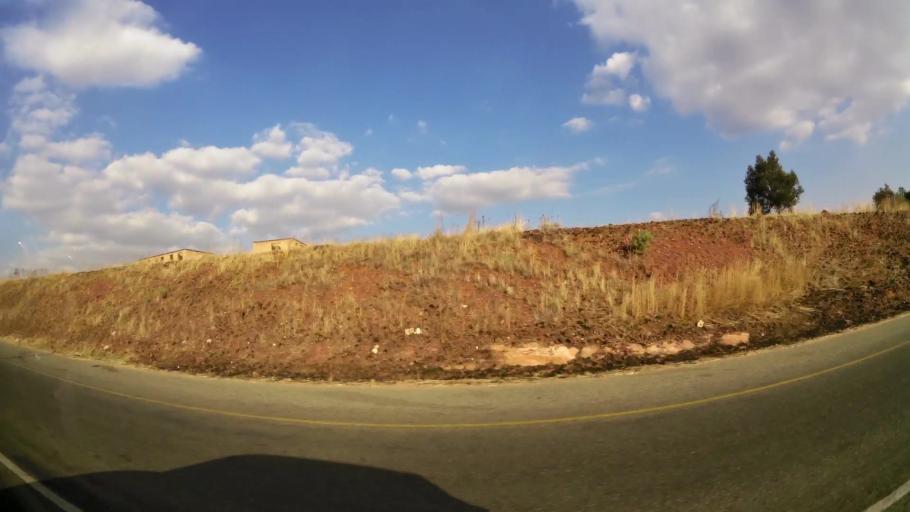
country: ZA
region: Gauteng
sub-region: West Rand District Municipality
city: Krugersdorp
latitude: -26.0840
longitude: 27.7534
